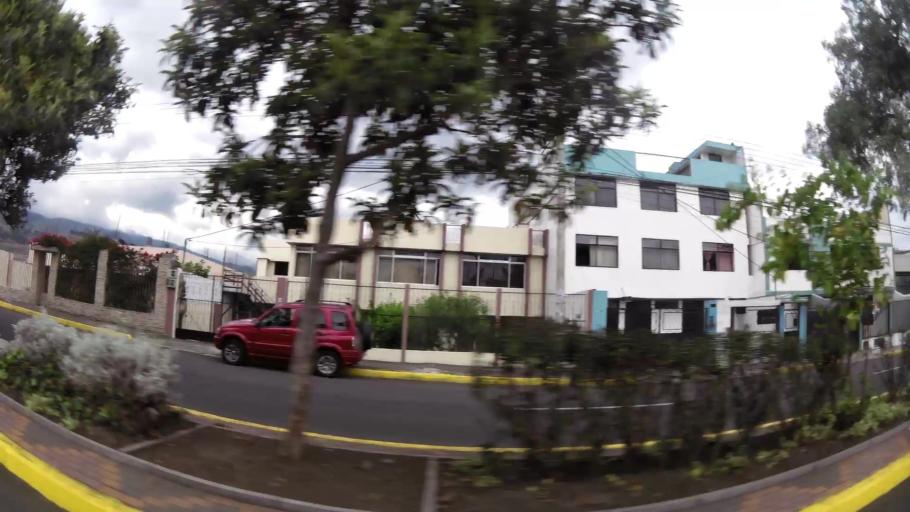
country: EC
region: Tungurahua
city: Ambato
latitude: -1.2318
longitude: -78.6151
